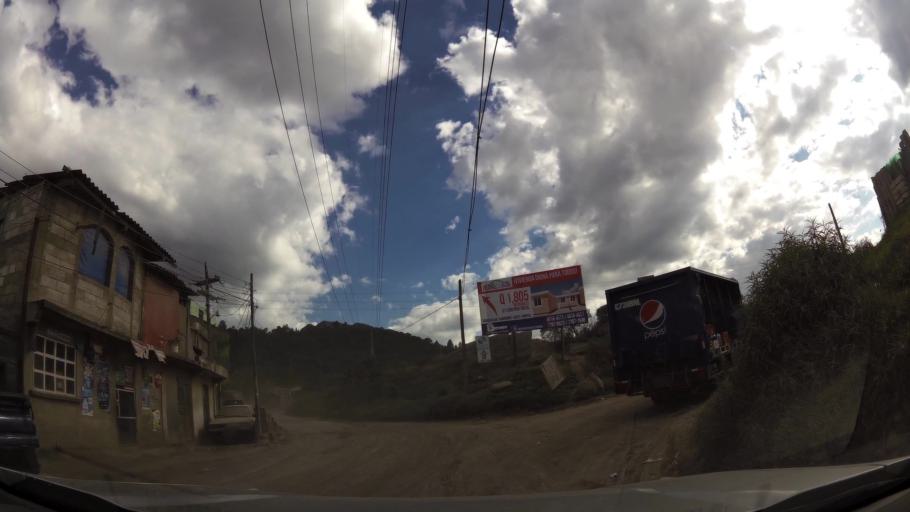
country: GT
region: Quetzaltenango
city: Quetzaltenango
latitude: 14.8282
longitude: -91.5369
